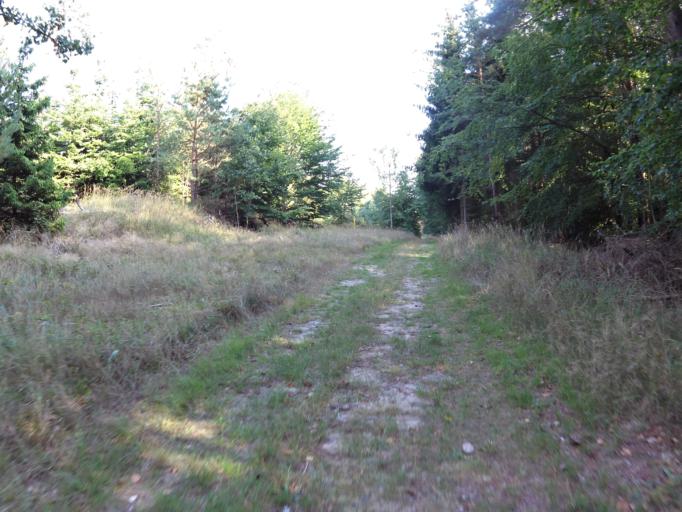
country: DE
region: Mecklenburg-Vorpommern
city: Loddin
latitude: 54.0060
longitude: 14.0543
